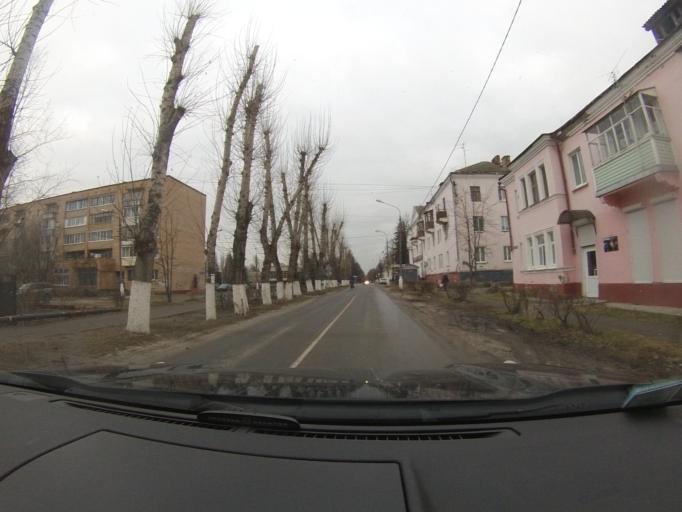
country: RU
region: Moskovskaya
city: Lopatinskiy
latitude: 55.3399
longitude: 38.7199
